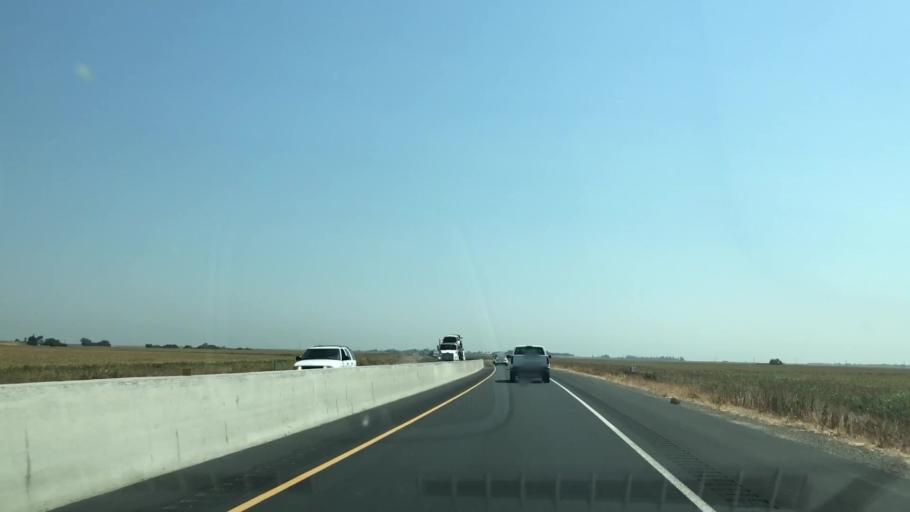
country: US
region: California
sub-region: Sacramento County
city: Walnut Grove
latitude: 38.1132
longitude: -121.5480
